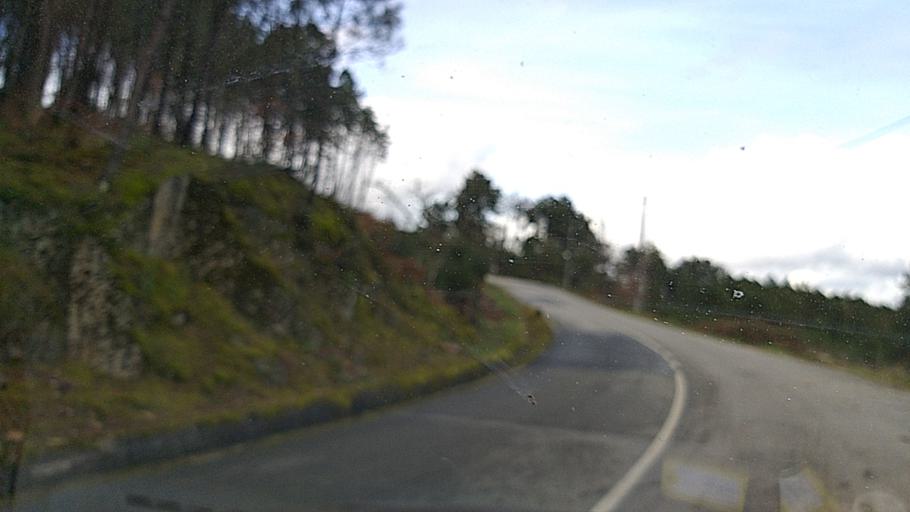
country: PT
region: Guarda
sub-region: Fornos de Algodres
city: Fornos de Algodres
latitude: 40.6679
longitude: -7.6110
